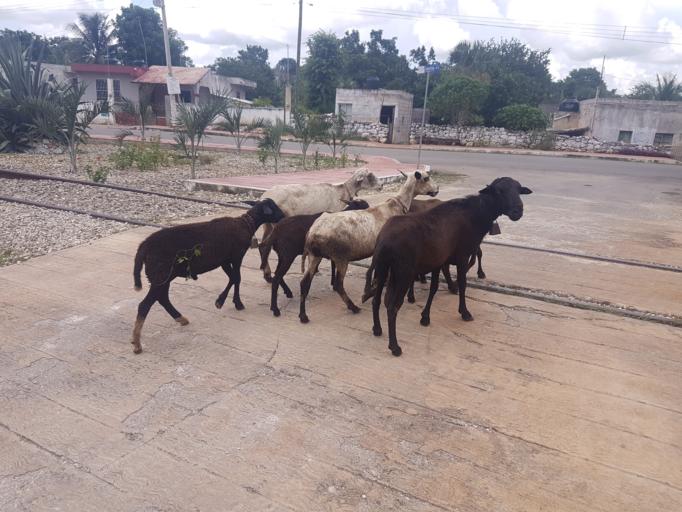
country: MX
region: Yucatan
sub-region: Uayma
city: Uayma
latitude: 20.7204
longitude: -88.3132
